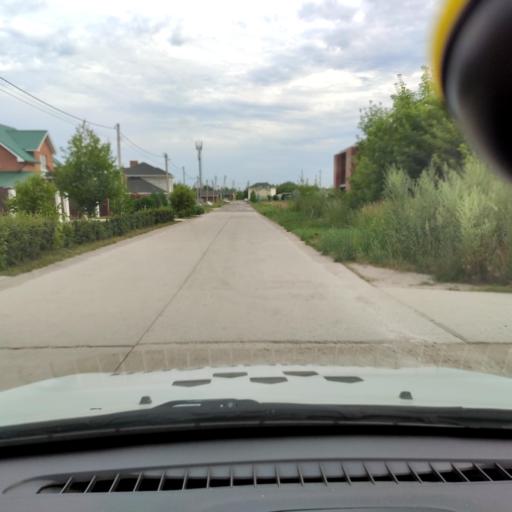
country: RU
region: Samara
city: Podstepki
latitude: 53.5764
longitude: 49.0813
